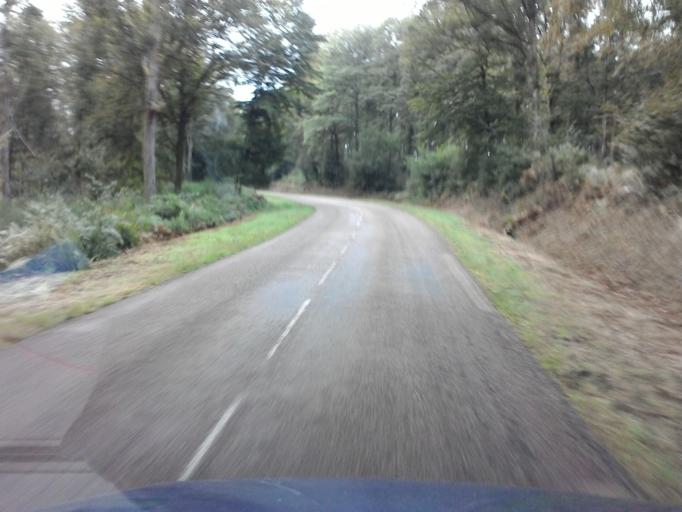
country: FR
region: Bourgogne
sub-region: Departement de la Nievre
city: Lormes
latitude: 47.2055
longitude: 3.8457
